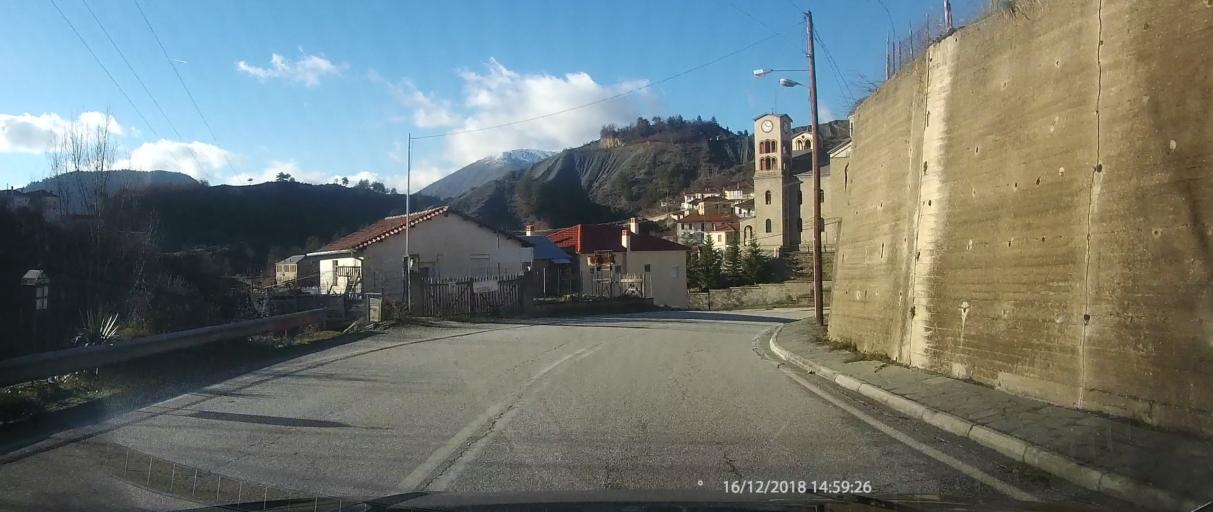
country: GR
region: West Macedonia
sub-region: Nomos Kastorias
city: Nestorio
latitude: 40.2217
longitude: 21.0224
